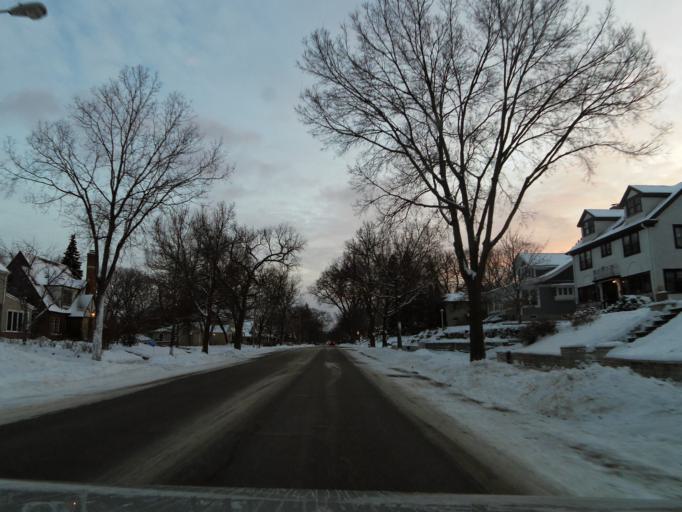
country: US
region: Minnesota
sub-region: Hennepin County
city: Saint Louis Park
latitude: 44.9313
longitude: -93.3214
